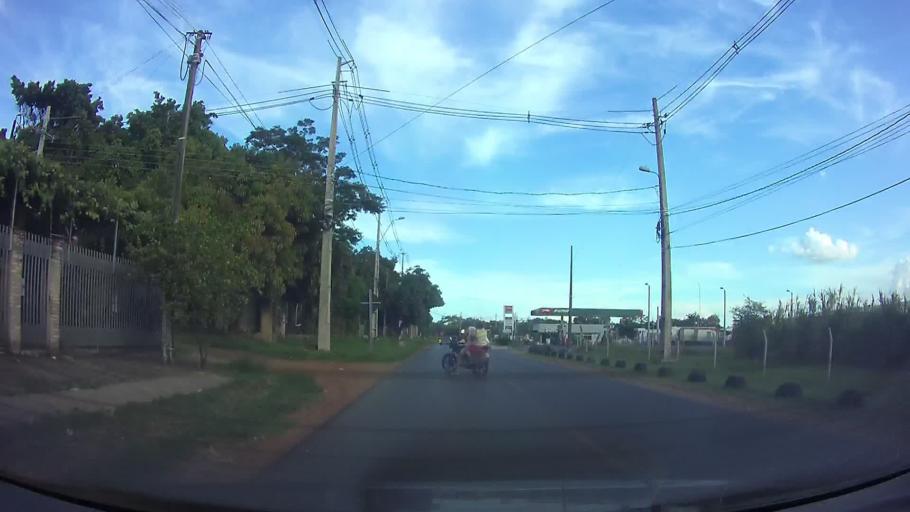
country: PY
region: Central
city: San Antonio
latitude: -25.4297
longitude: -57.5547
